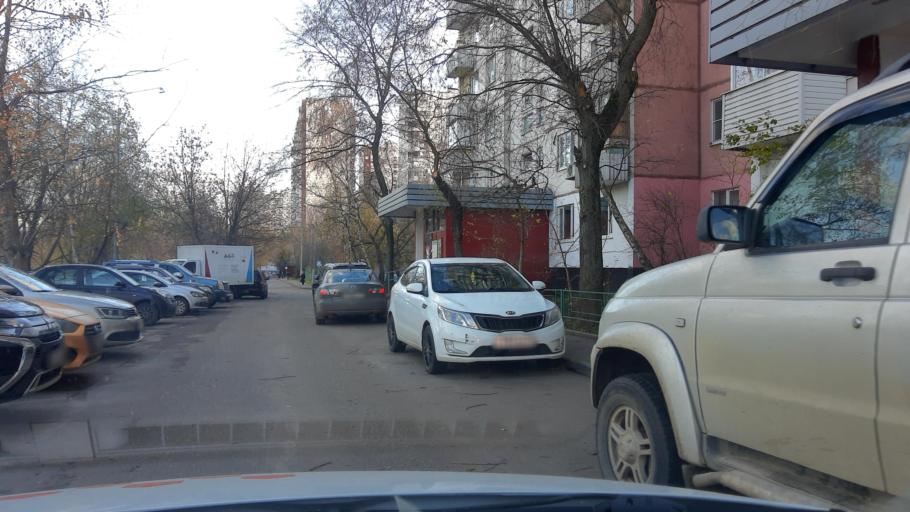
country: RU
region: Moscow
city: Orekhovo-Borisovo
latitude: 55.6300
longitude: 37.7356
